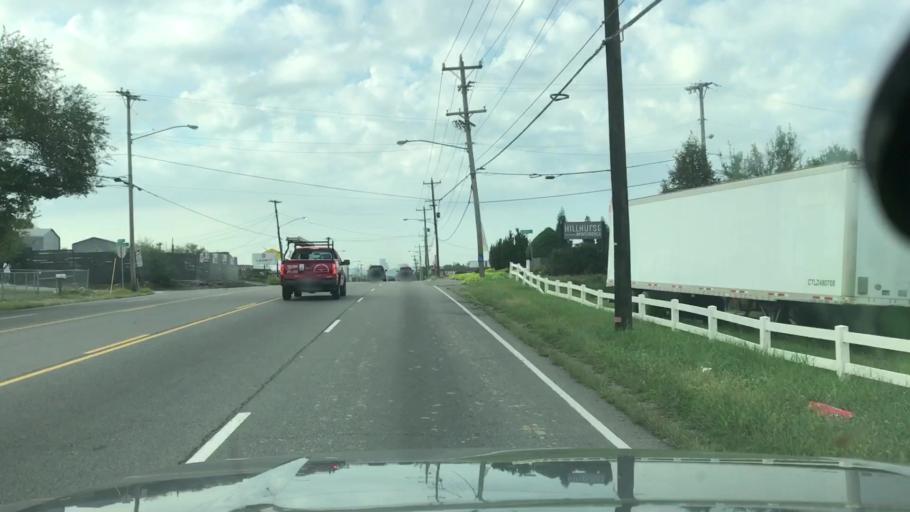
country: US
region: Tennessee
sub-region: Davidson County
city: Nashville
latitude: 36.2243
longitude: -86.7609
